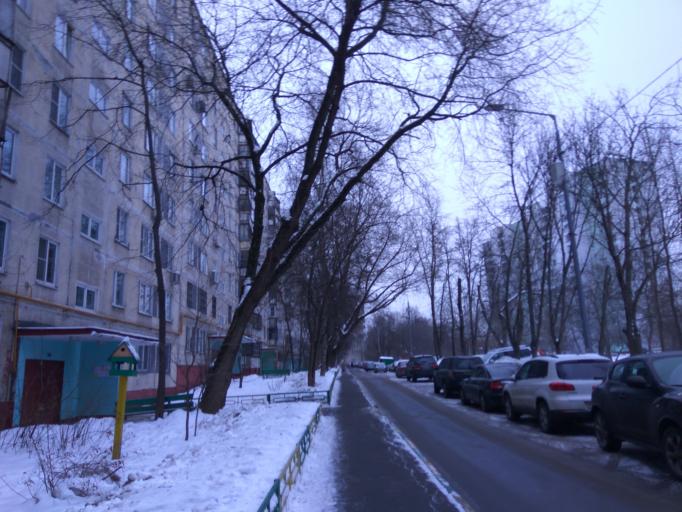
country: RU
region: Moscow
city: Ivanovskoye
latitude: 55.7705
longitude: 37.8238
